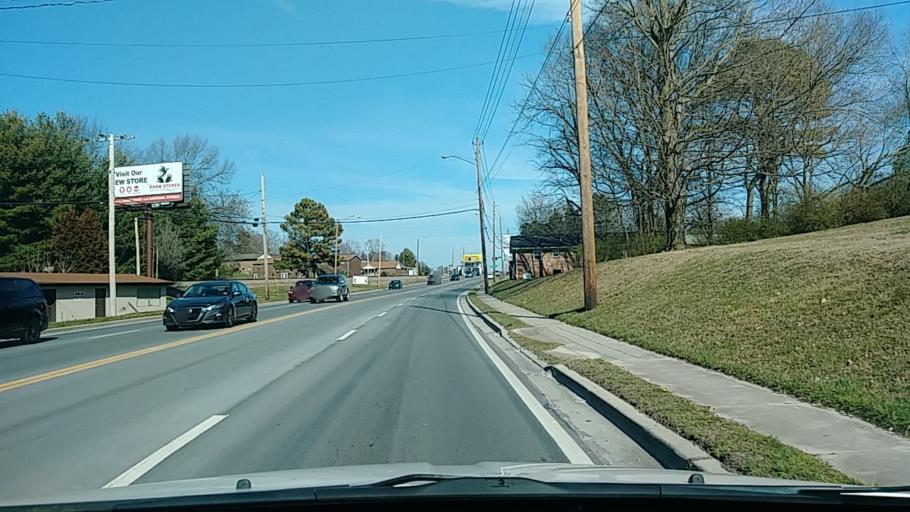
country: US
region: Tennessee
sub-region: Hamblen County
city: Morristown
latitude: 36.2189
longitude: -83.2726
